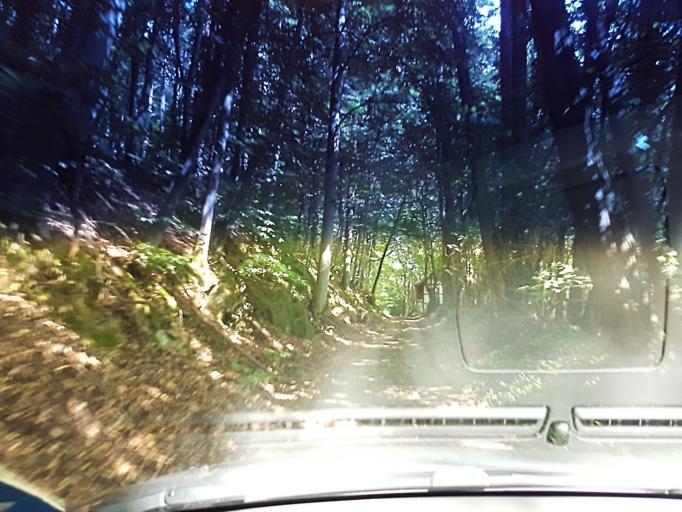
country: DE
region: Bavaria
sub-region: Upper Franconia
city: Litzendorf
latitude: 49.8681
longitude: 11.0517
